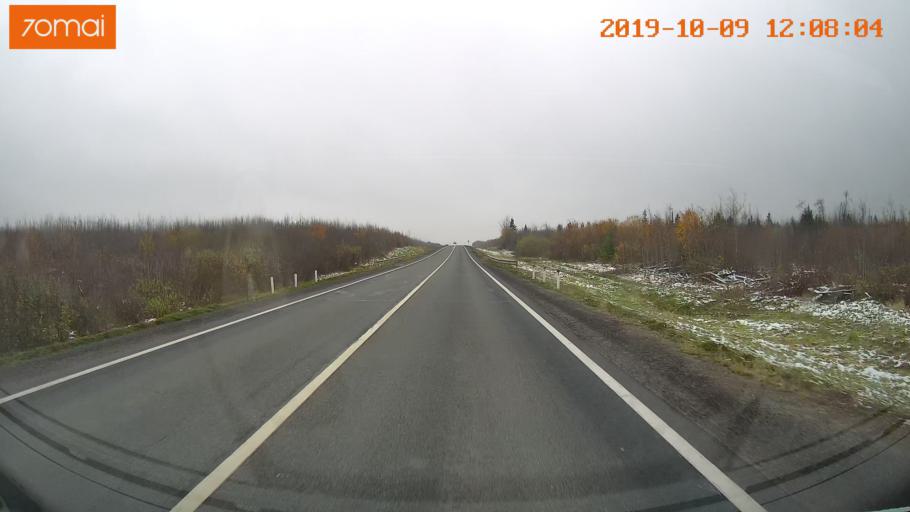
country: RU
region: Jaroslavl
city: Prechistoye
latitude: 58.5915
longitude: 40.3452
